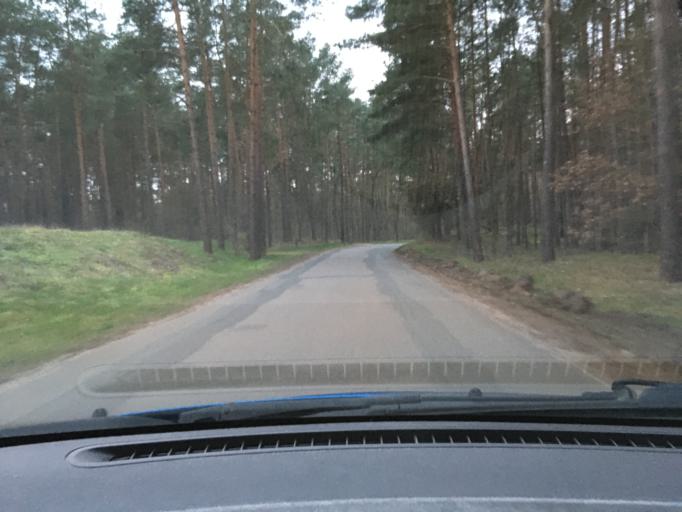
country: DE
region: Lower Saxony
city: Bleckede
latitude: 53.2917
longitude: 10.7011
